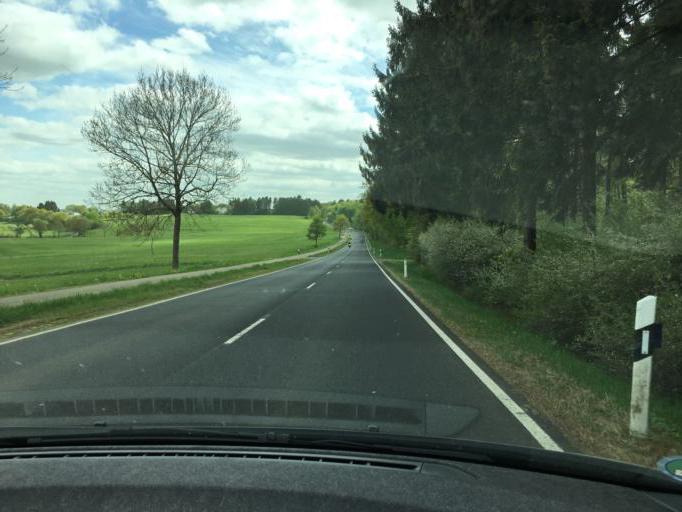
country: DE
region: Rheinland-Pfalz
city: Kirchsahr
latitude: 50.5285
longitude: 6.8521
